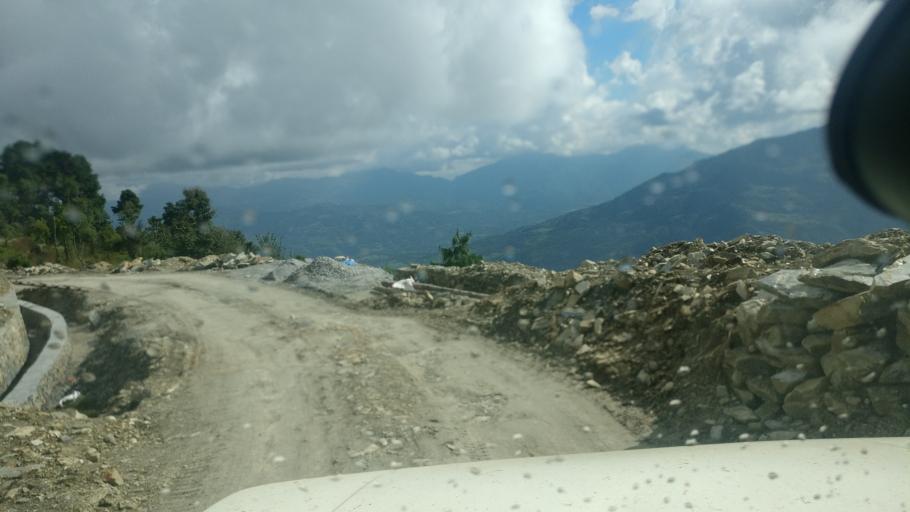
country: NP
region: Western Region
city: Baglung
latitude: 28.2834
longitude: 83.6393
